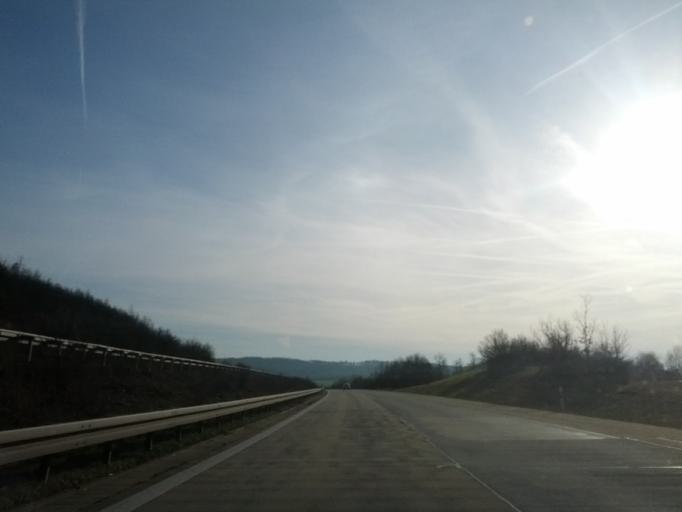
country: DE
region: Bavaria
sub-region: Regierungsbezirk Mittelfranken
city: Neusitz
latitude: 49.3609
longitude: 10.2149
